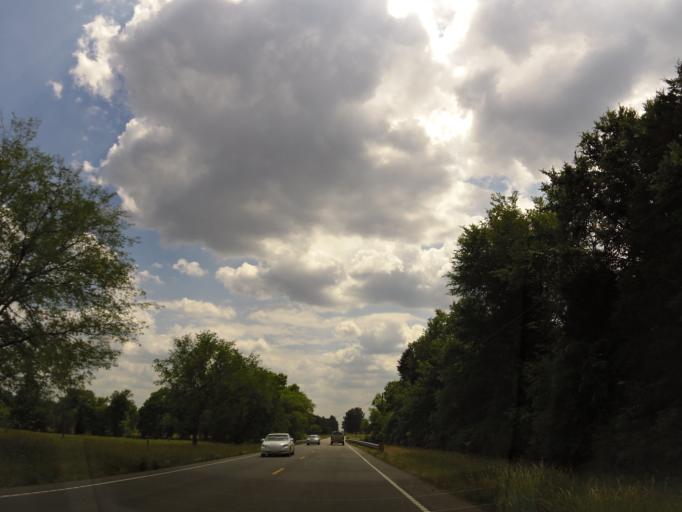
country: US
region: Tennessee
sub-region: Sequatchie County
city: Dunlap
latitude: 35.4321
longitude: -85.3522
